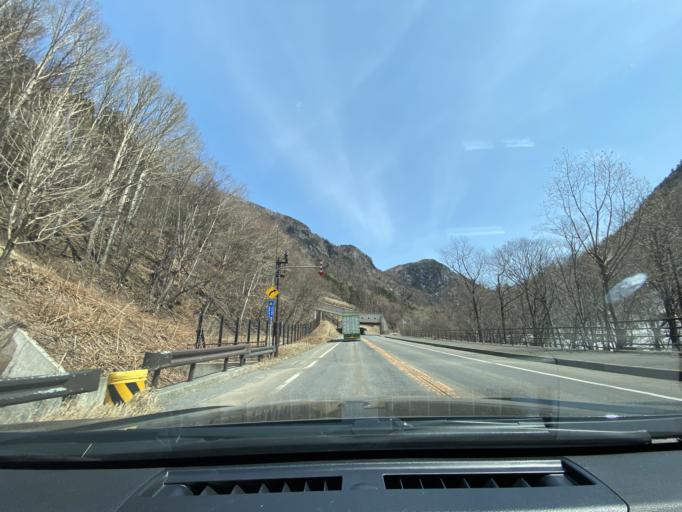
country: JP
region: Hokkaido
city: Kamikawa
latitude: 43.7264
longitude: 142.9630
